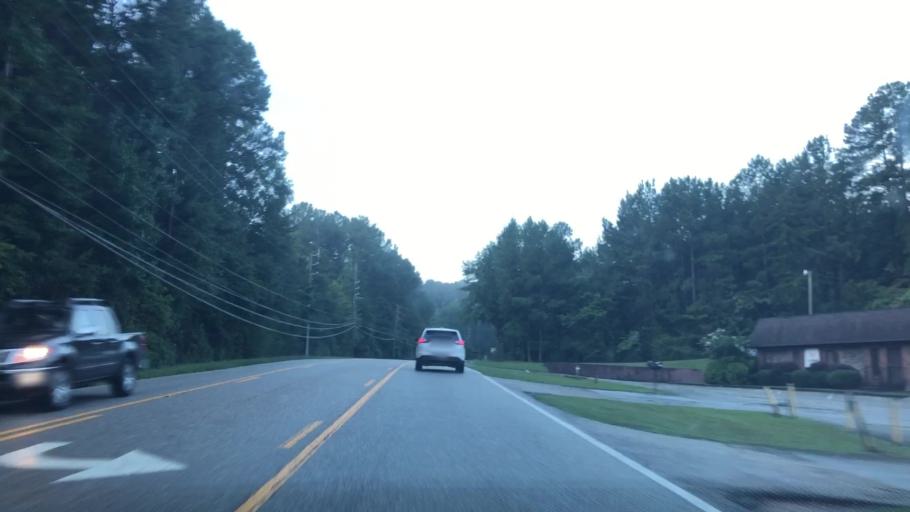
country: US
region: Alabama
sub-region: Shelby County
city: Indian Springs Village
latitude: 33.3705
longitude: -86.7595
